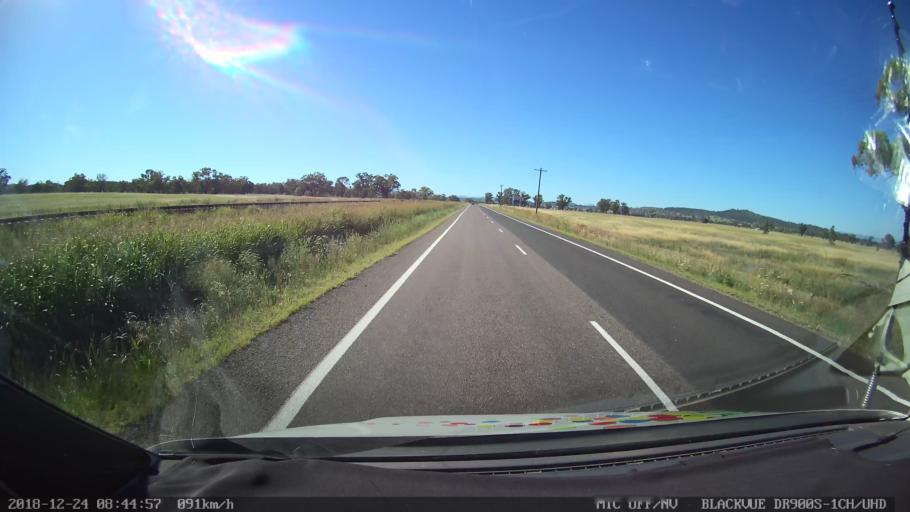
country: AU
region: New South Wales
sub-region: Liverpool Plains
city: Quirindi
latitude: -31.4087
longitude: 150.6503
